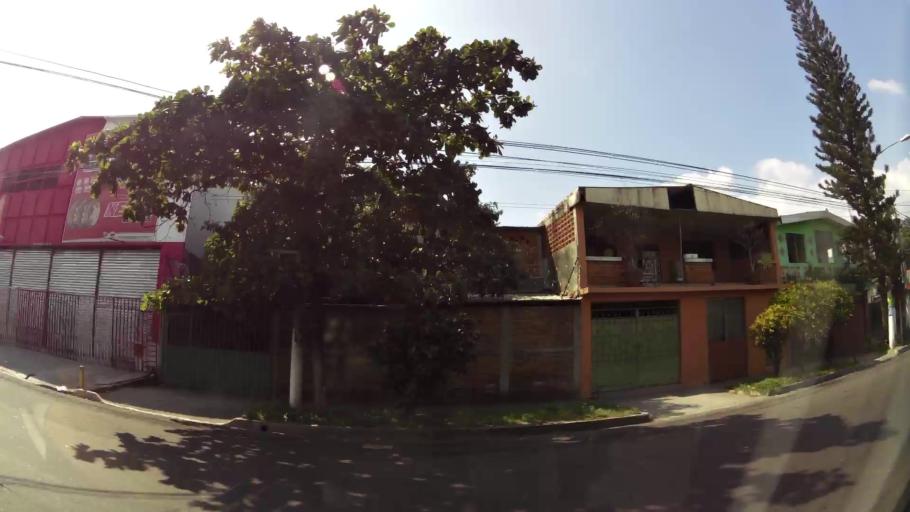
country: SV
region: San Salvador
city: Mejicanos
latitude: 13.7207
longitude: -89.2168
